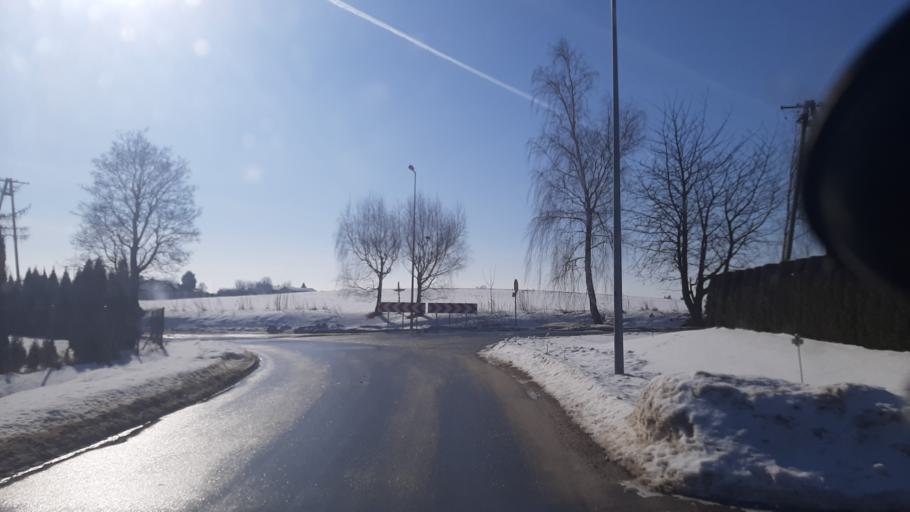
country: PL
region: Lublin Voivodeship
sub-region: Powiat lubelski
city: Garbow
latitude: 51.3058
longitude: 22.3057
